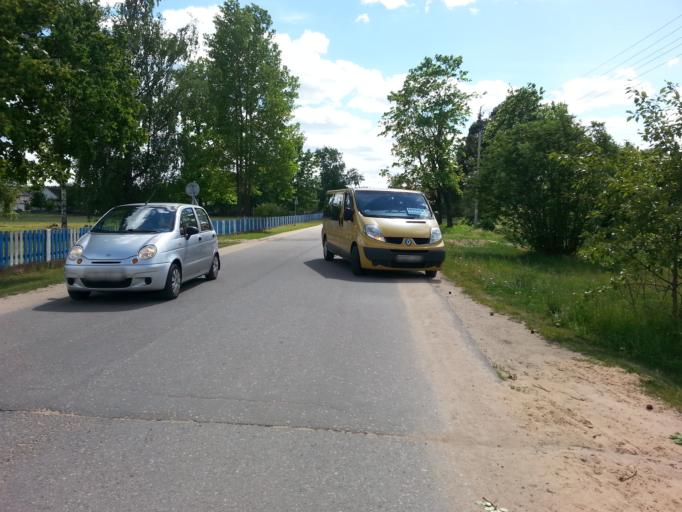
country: BY
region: Minsk
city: Narach
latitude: 54.9303
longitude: 26.6843
